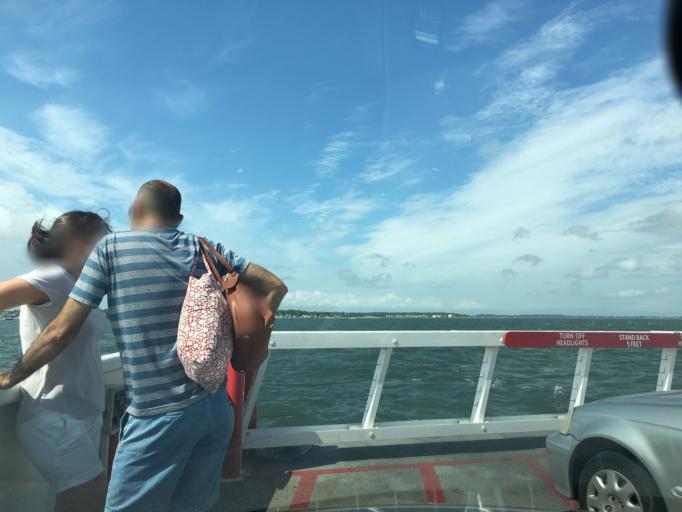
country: US
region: New York
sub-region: Suffolk County
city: Shelter Island Heights
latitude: 41.0929
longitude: -72.3577
